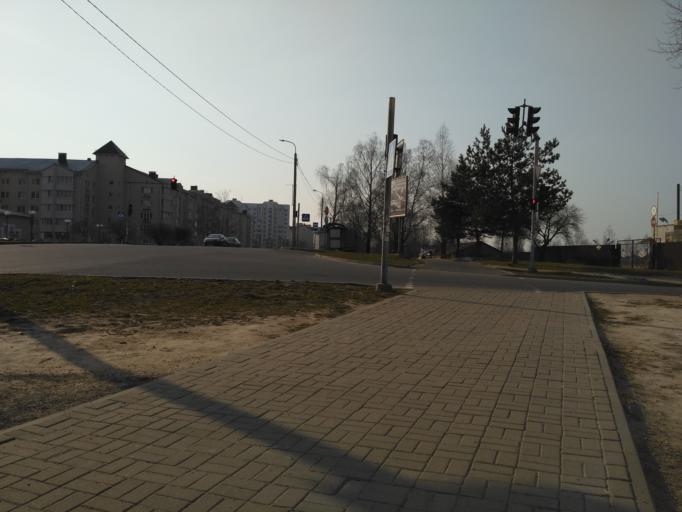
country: BY
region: Minsk
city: Zaslawye
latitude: 54.0122
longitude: 27.2658
